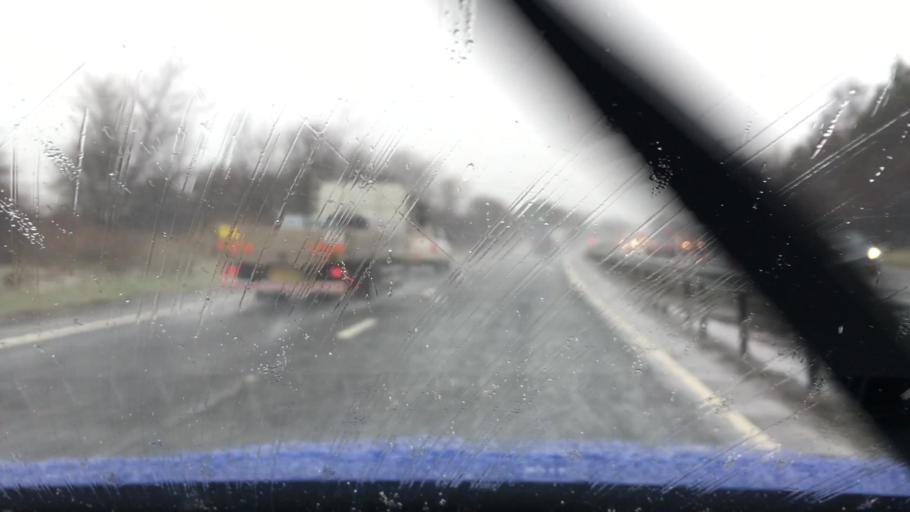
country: GB
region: Scotland
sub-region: Edinburgh
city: Currie
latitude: 55.9151
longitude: -3.2972
